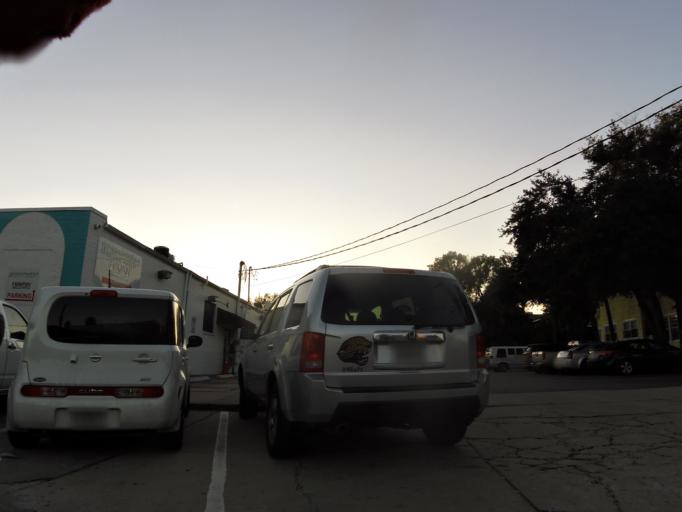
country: US
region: Florida
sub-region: Duval County
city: Jacksonville
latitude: 30.3144
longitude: -81.6815
